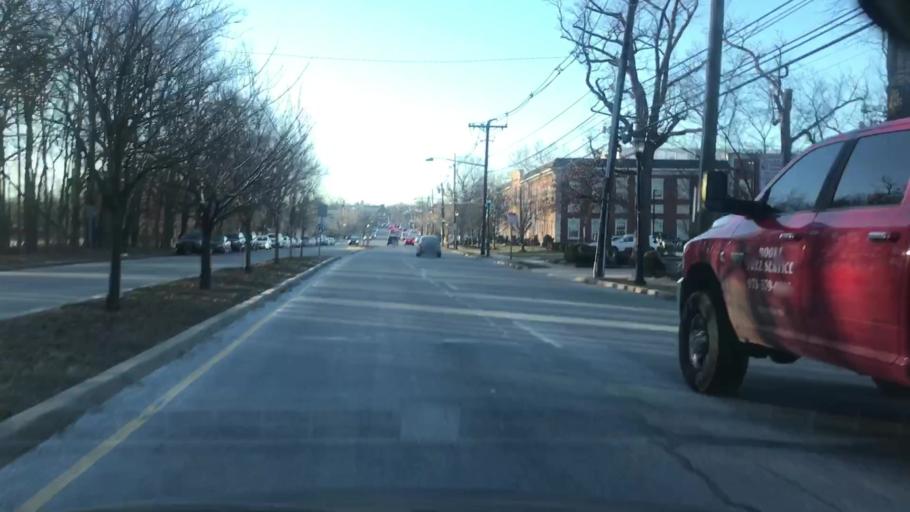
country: US
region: New Jersey
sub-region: Essex County
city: Northfield
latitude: 40.7733
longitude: -74.3194
